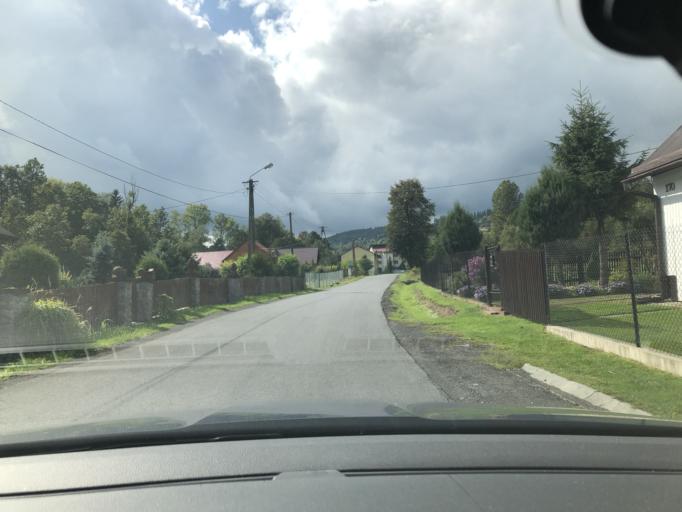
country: PL
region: Lesser Poland Voivodeship
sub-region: Powiat suski
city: Lachowice
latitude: 49.7078
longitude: 19.4267
